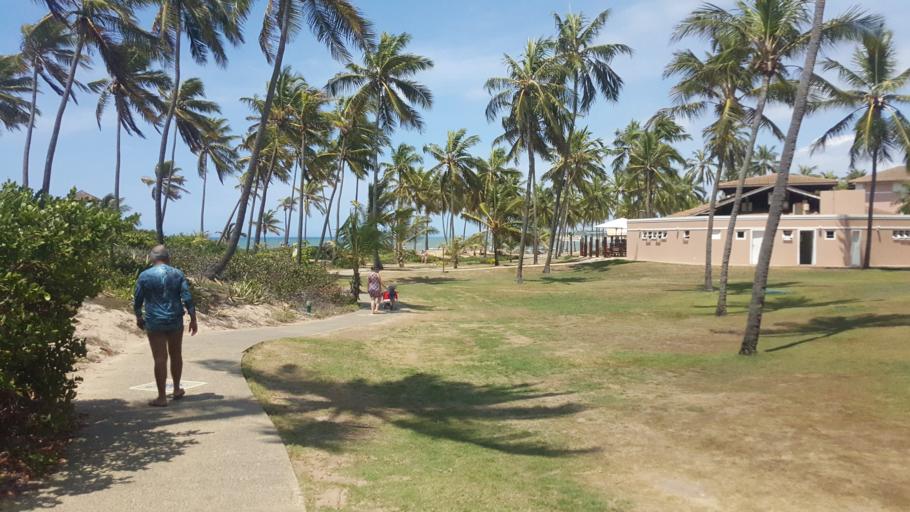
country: BR
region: Bahia
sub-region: Mata De Sao Joao
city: Mata de Sao Joao
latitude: -12.4386
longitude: -37.9207
